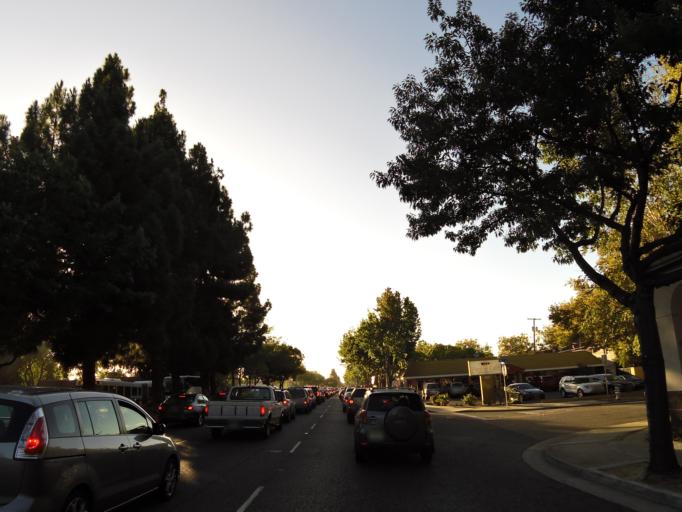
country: US
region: California
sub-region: Santa Clara County
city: Mountain View
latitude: 37.3847
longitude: -122.0815
